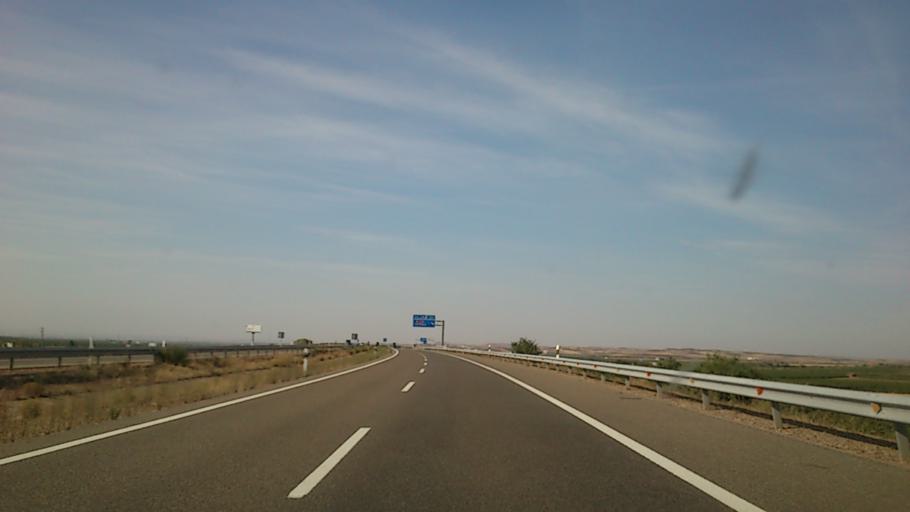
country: ES
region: Aragon
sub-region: Provincia de Zaragoza
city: Carinena
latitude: 41.3601
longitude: -1.2029
